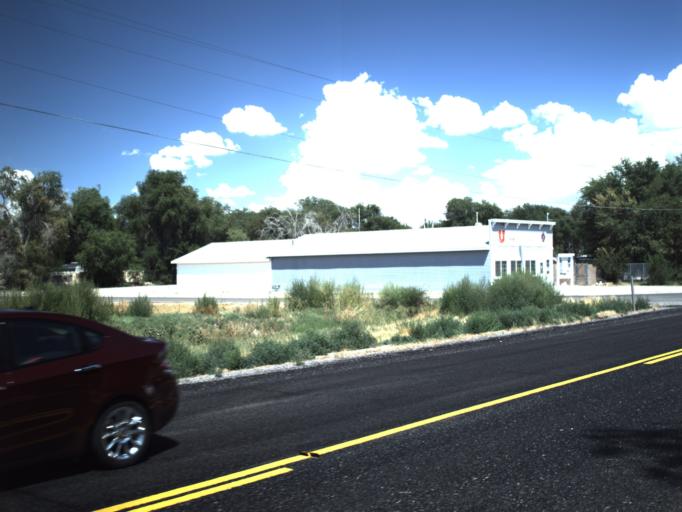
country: US
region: Utah
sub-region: Millard County
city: Delta
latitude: 39.3524
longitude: -112.5905
